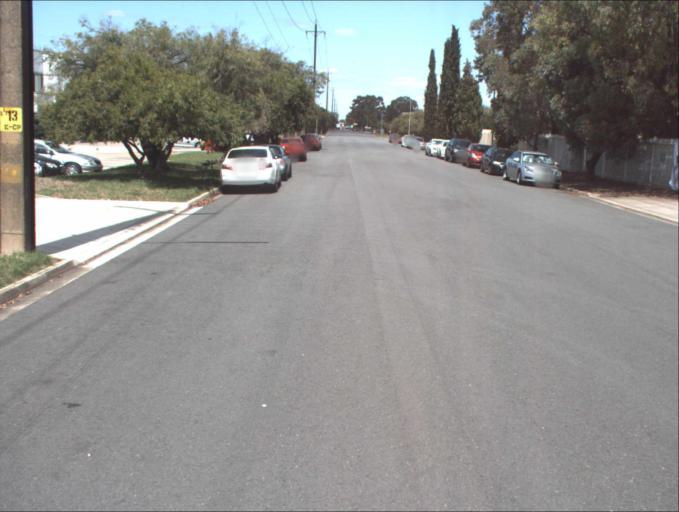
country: AU
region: South Australia
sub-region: Port Adelaide Enfield
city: Blair Athol
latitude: -34.8508
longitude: 138.5697
